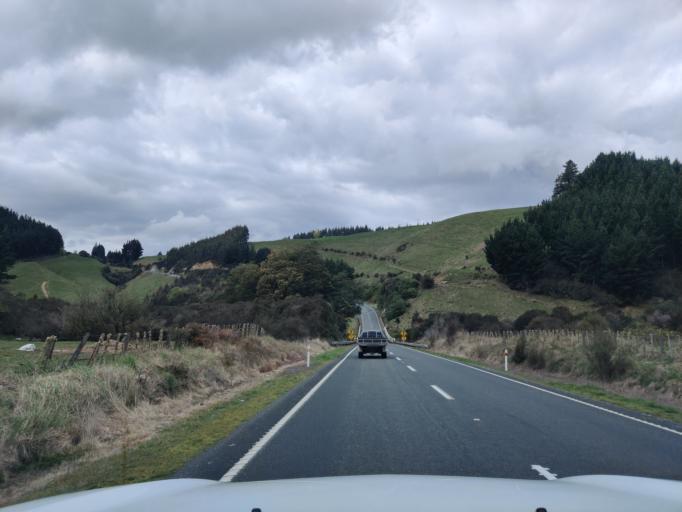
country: NZ
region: Manawatu-Wanganui
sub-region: Ruapehu District
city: Waiouru
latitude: -39.4985
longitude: 175.2888
